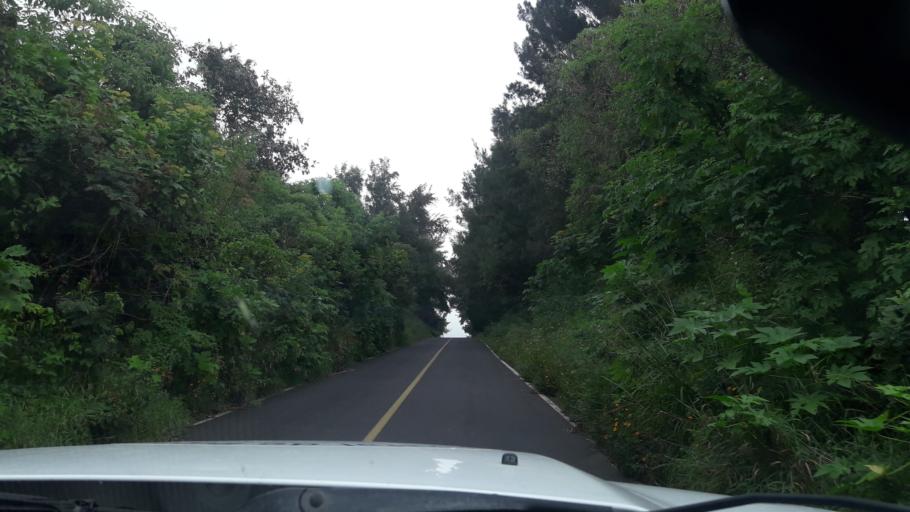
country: MX
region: Colima
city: Suchitlan
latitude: 19.4108
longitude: -103.6449
